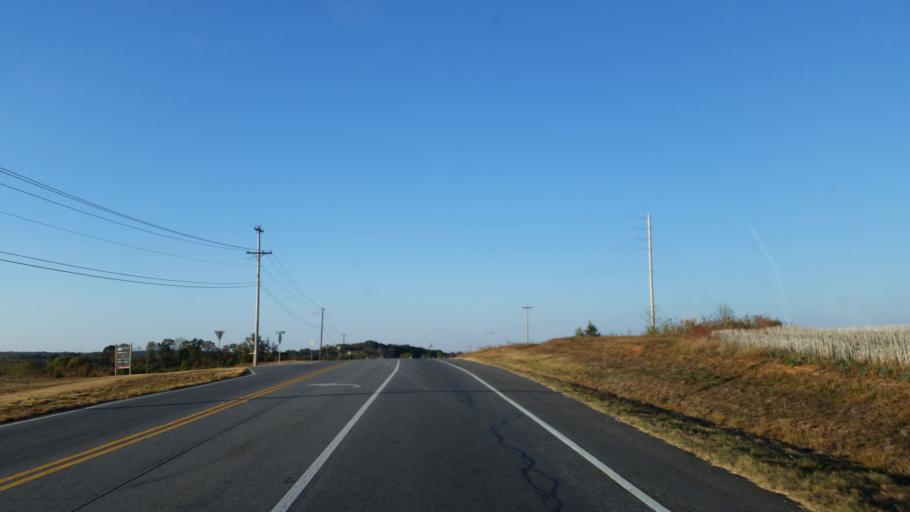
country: US
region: Georgia
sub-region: Bartow County
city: Adairsville
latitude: 34.4006
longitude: -84.9347
